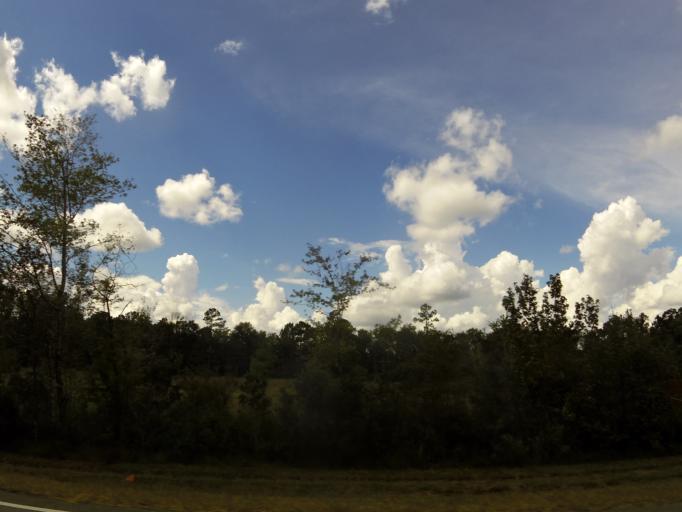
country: US
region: Georgia
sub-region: Brantley County
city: Nahunta
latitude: 31.0783
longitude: -82.0106
